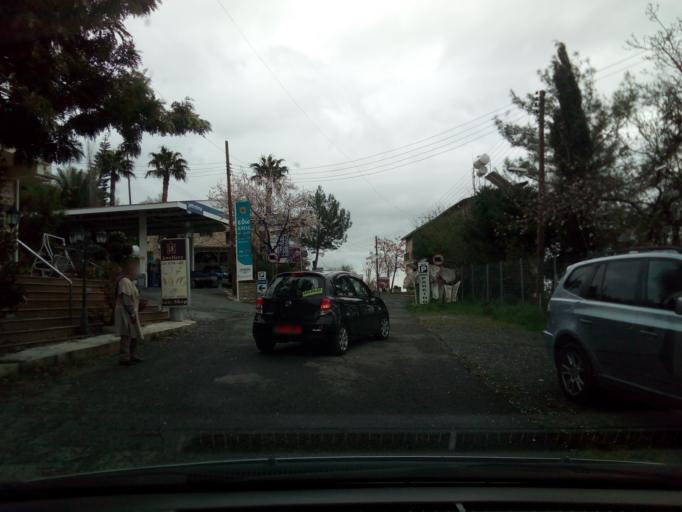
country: CY
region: Lefkosia
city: Lythrodontas
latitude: 34.8624
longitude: 33.3067
